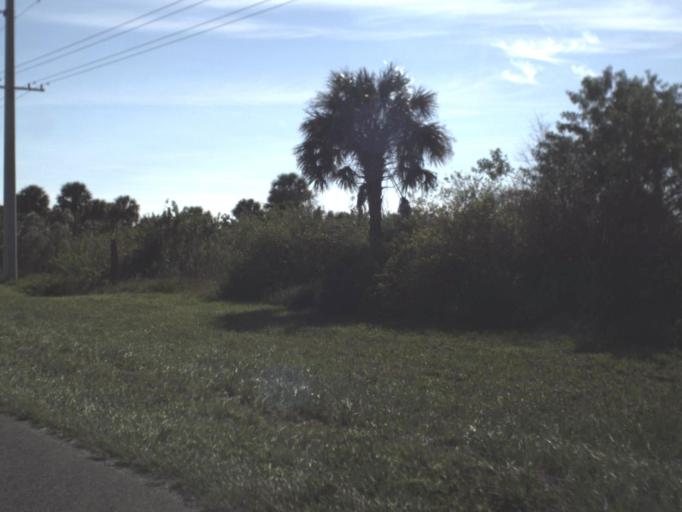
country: US
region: Florida
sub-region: Glades County
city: Moore Haven
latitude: 26.7735
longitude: -81.0831
